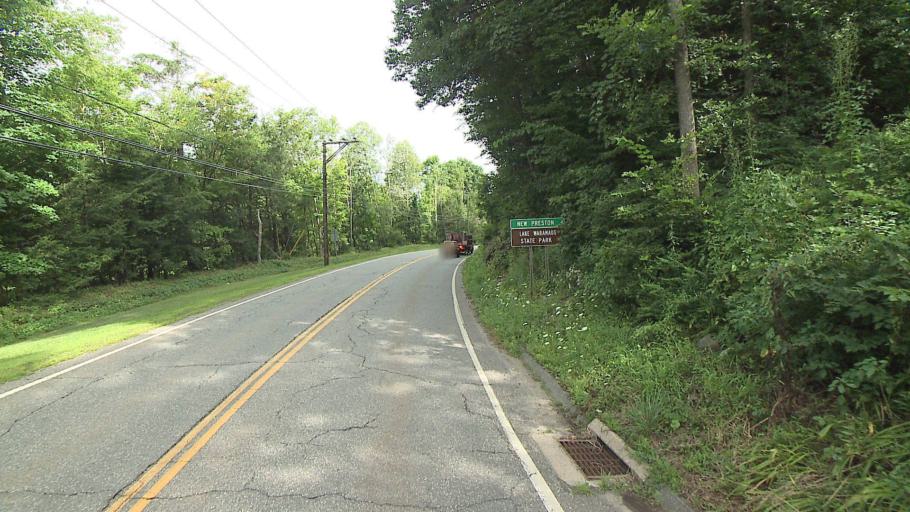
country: US
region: Connecticut
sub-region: Litchfield County
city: New Preston
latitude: 41.6458
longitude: -73.3175
